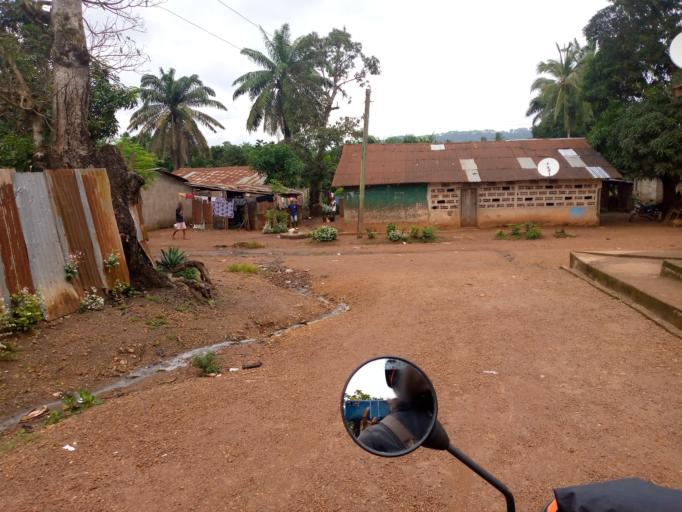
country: SL
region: Eastern Province
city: Kenema
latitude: 7.8629
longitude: -11.1887
